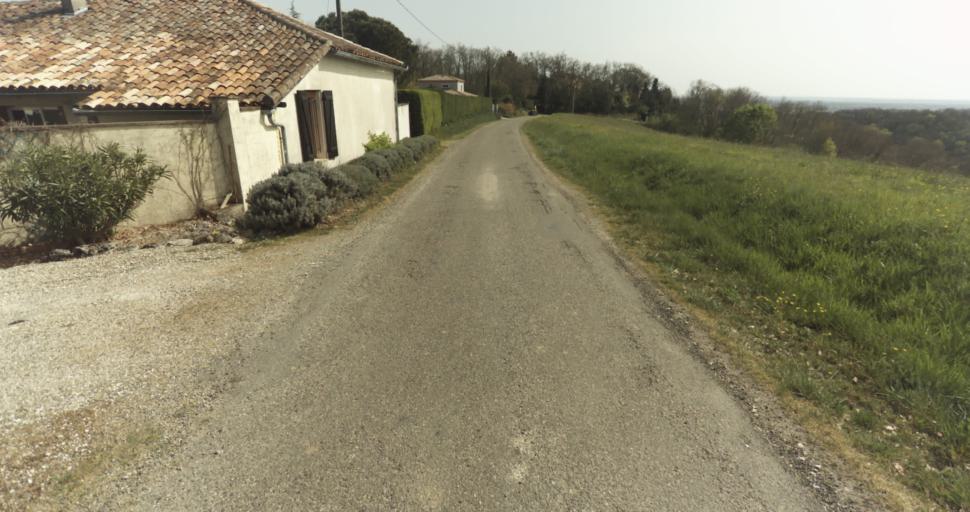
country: FR
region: Midi-Pyrenees
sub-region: Departement du Tarn-et-Garonne
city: Moissac
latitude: 44.1355
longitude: 1.1466
